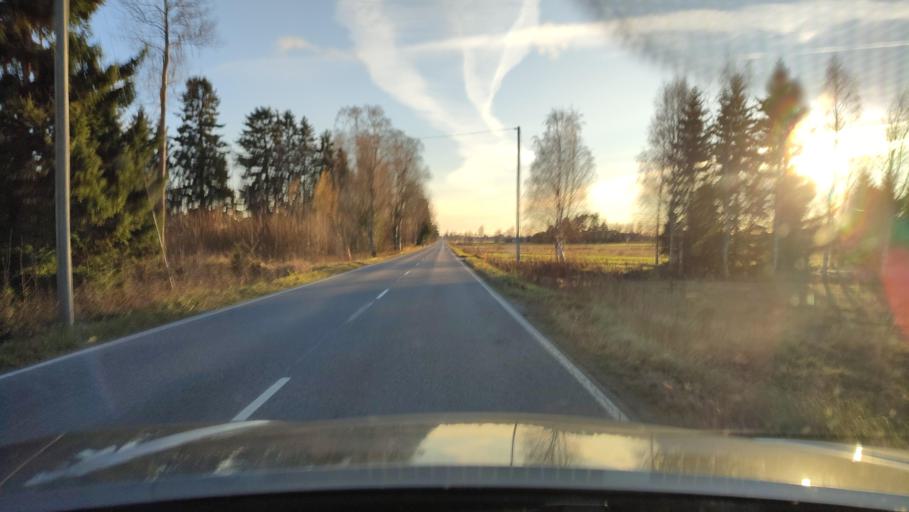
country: FI
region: Ostrobothnia
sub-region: Sydosterbotten
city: Naerpes
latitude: 62.6407
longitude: 21.5024
